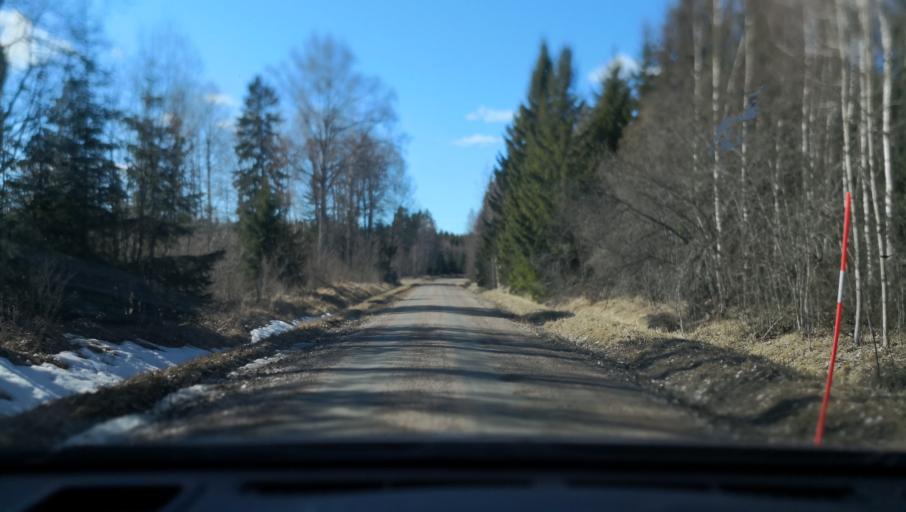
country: SE
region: Vaestmanland
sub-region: Sala Kommun
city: Sala
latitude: 60.1156
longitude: 16.6747
